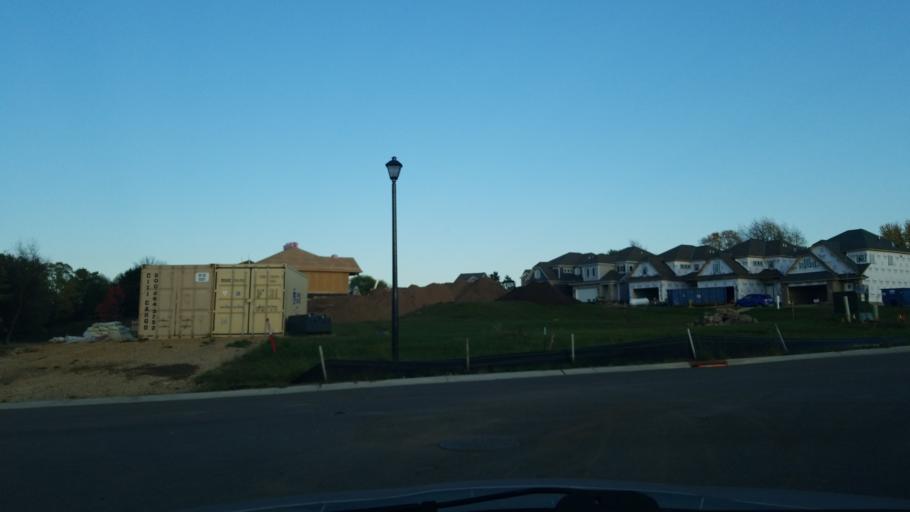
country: US
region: Wisconsin
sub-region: Saint Croix County
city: Hudson
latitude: 44.9687
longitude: -92.7289
